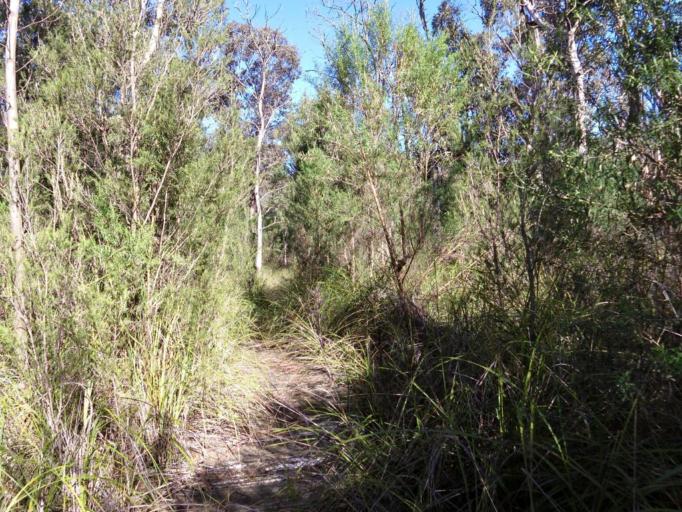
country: AU
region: Victoria
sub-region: Yarra Ranges
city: Lysterfield
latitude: -37.9609
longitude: 145.2945
